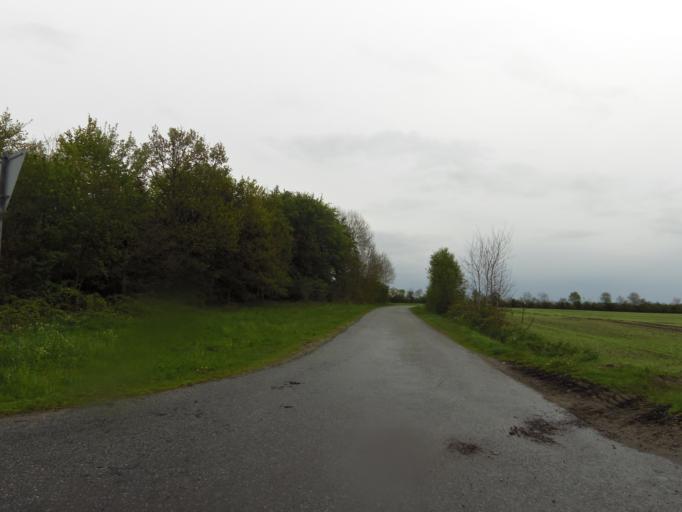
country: DK
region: South Denmark
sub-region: Tonder Kommune
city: Sherrebek
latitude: 55.2077
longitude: 8.8882
